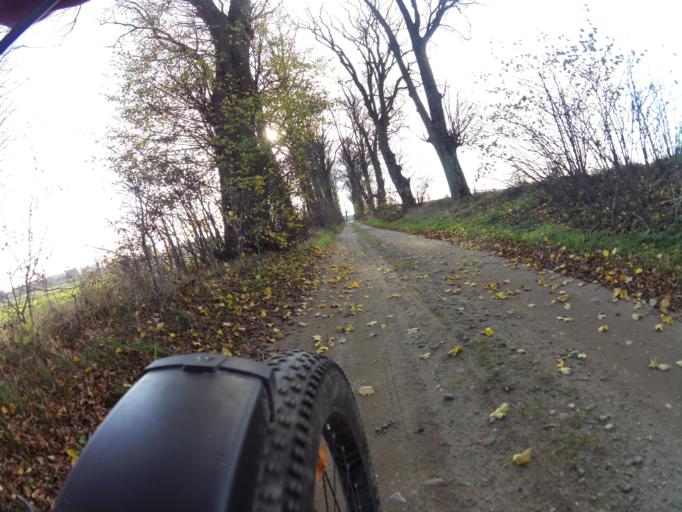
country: PL
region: Pomeranian Voivodeship
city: Strzelno
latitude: 54.7513
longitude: 18.2901
